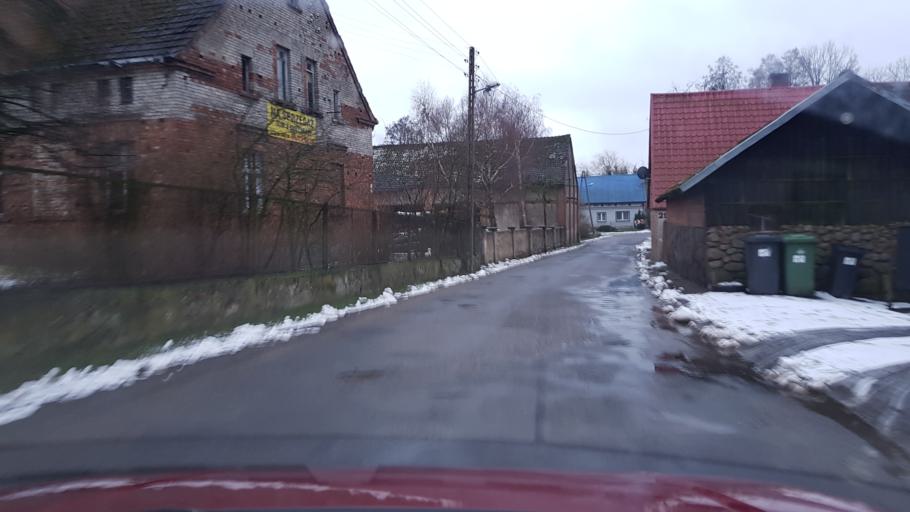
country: PL
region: West Pomeranian Voivodeship
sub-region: Powiat goleniowski
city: Mosty
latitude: 53.4975
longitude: 14.8990
